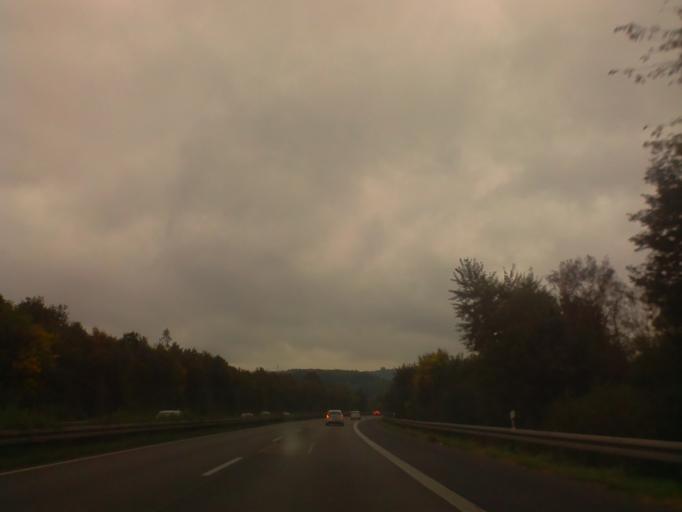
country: DE
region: Hesse
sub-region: Regierungsbezirk Darmstadt
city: Wachtersbach
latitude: 50.2332
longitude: 9.2859
